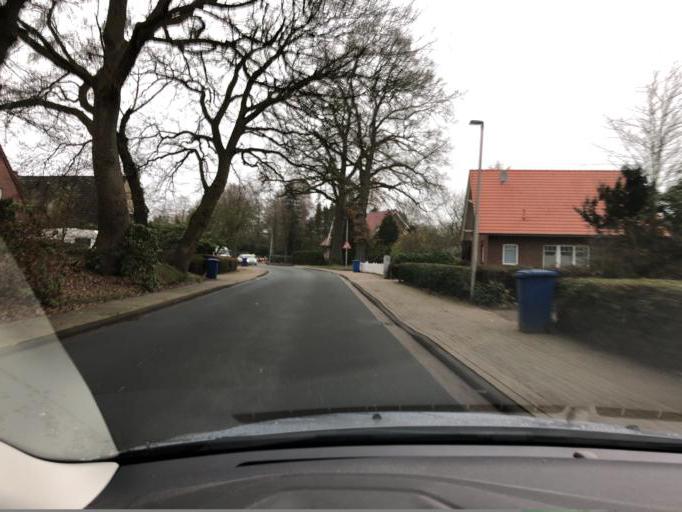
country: DE
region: Lower Saxony
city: Bad Zwischenahn
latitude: 53.1728
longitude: 8.0111
